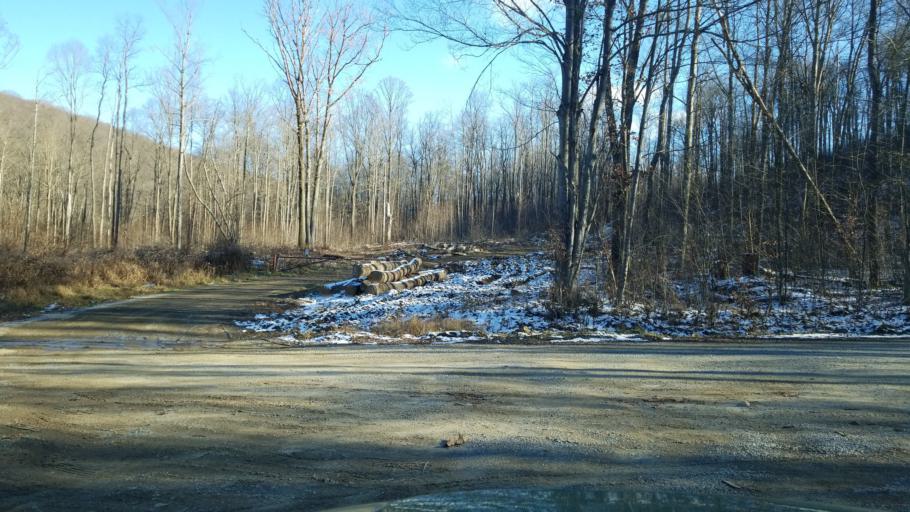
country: US
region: Pennsylvania
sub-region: Jefferson County
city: Brockway
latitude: 41.3004
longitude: -78.8261
